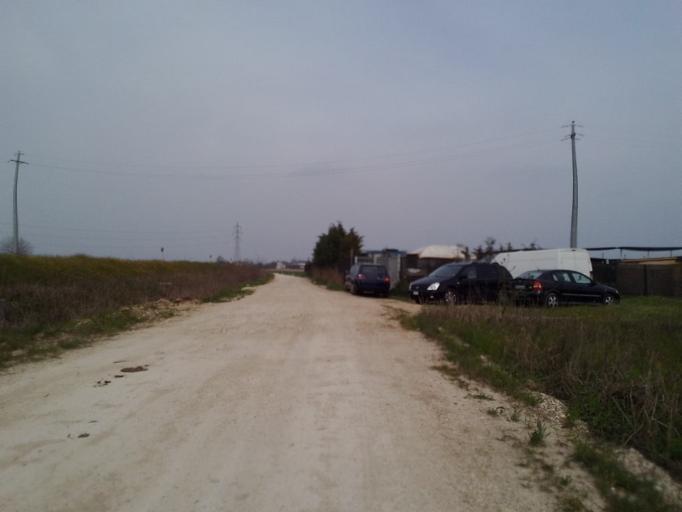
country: IT
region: Veneto
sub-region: Provincia di Verona
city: Povegliano Veronese
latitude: 45.3650
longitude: 10.8878
